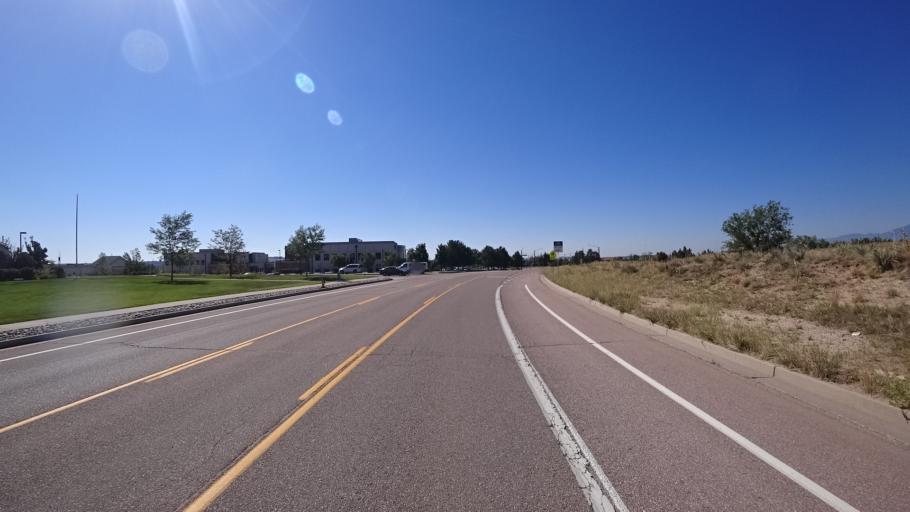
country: US
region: Colorado
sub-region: El Paso County
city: Black Forest
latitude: 38.9564
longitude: -104.7329
